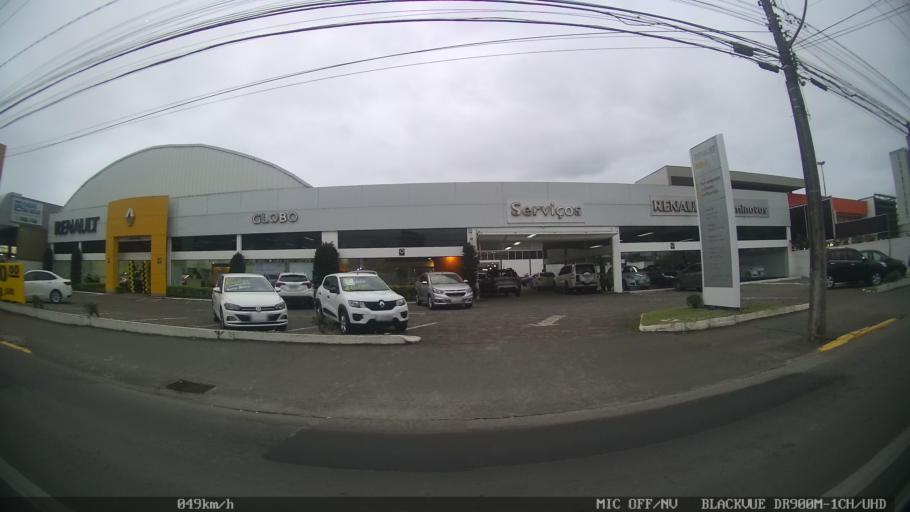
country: BR
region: Santa Catarina
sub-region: Joinville
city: Joinville
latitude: -26.2809
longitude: -48.8494
